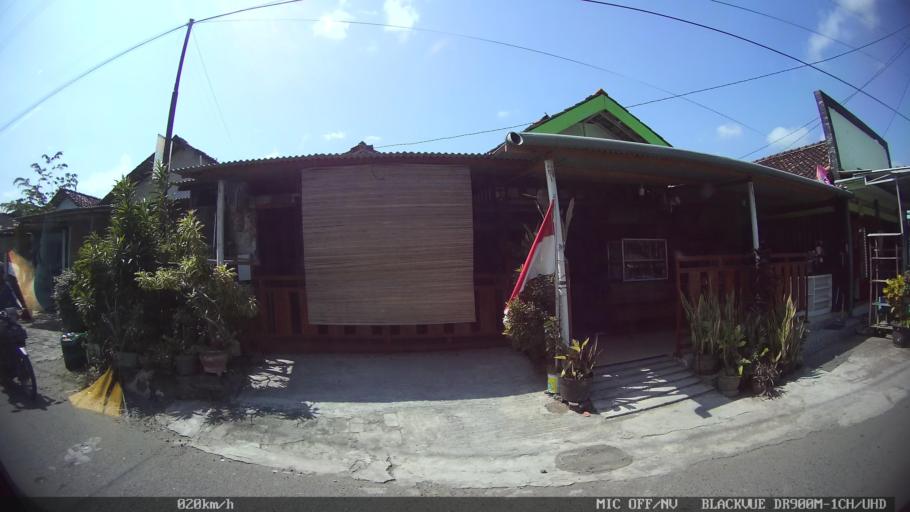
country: ID
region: Daerah Istimewa Yogyakarta
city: Pundong
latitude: -8.0200
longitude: 110.3247
